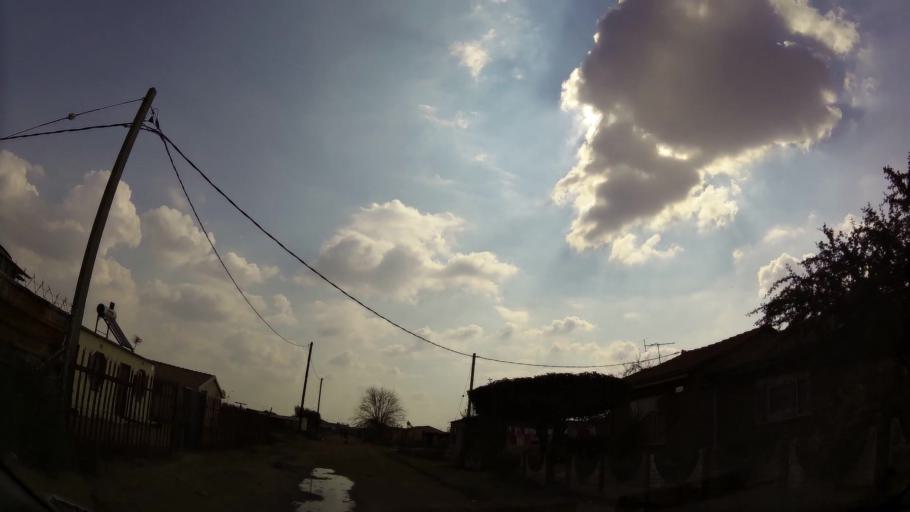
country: ZA
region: Gauteng
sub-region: Ekurhuleni Metropolitan Municipality
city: Springs
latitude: -26.1277
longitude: 28.4781
